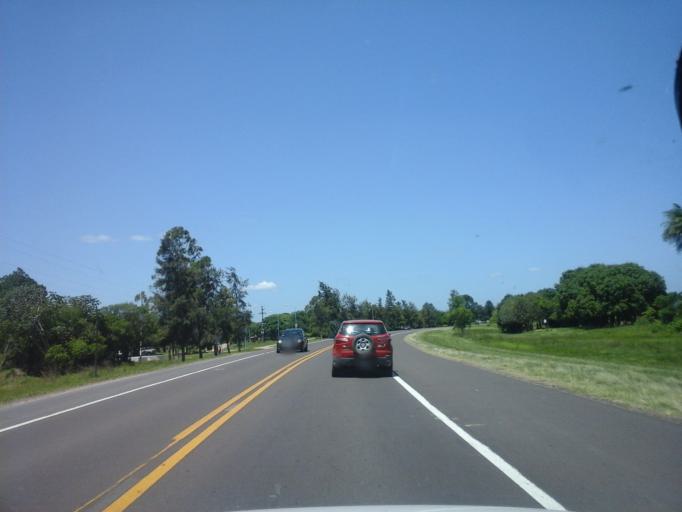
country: AR
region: Corrientes
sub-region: Departamento de San Cosme
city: San Cosme
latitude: -27.3773
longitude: -58.5116
